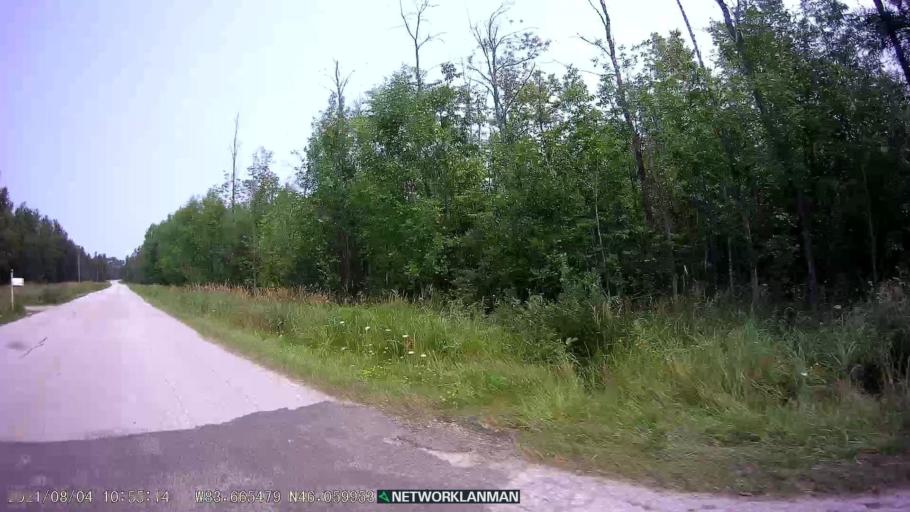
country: CA
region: Ontario
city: Thessalon
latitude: 46.0611
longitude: -83.6656
